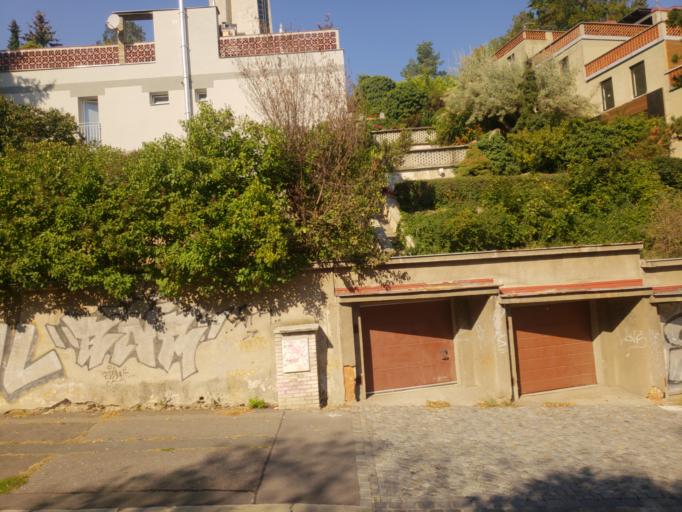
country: CZ
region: Praha
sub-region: Praha 1
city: Mala Strana
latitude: 50.0771
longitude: 14.3897
